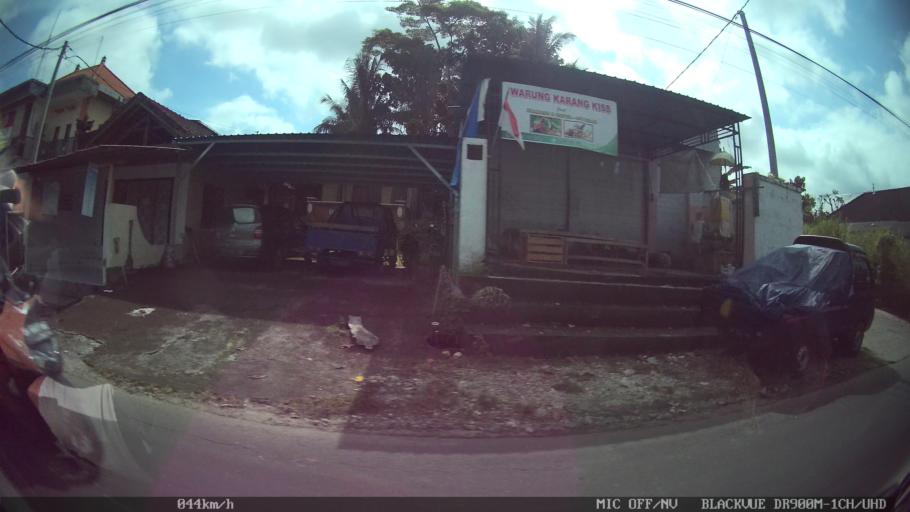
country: ID
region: Bali
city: Banjar Pesalakan
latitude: -8.5091
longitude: 115.3130
